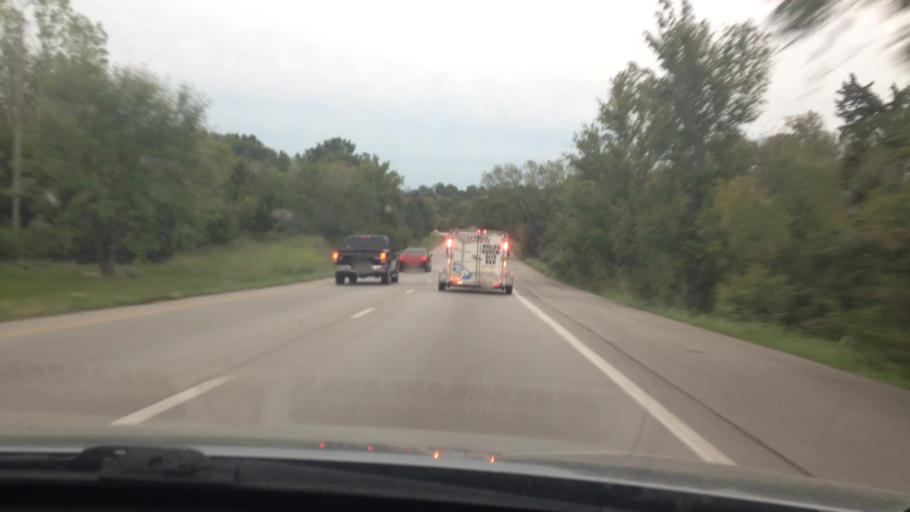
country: US
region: Missouri
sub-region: Jackson County
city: Raytown
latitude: 38.9706
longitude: -94.4412
